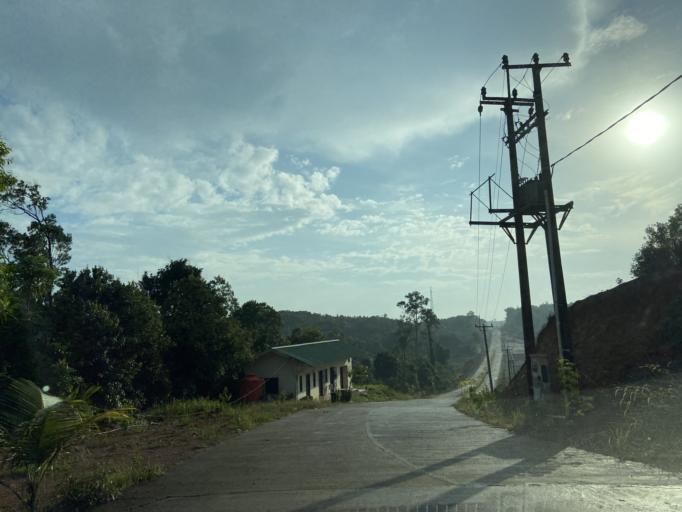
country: ID
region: Riau Islands
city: Tanjungpinang
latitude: 0.8944
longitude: 104.1233
